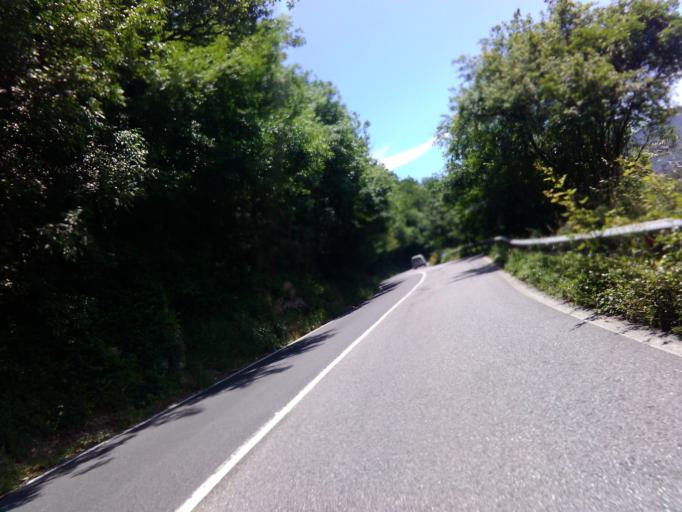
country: IT
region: Tuscany
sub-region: Provincia di Massa-Carrara
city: Barbarasco
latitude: 44.2669
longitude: 9.9542
